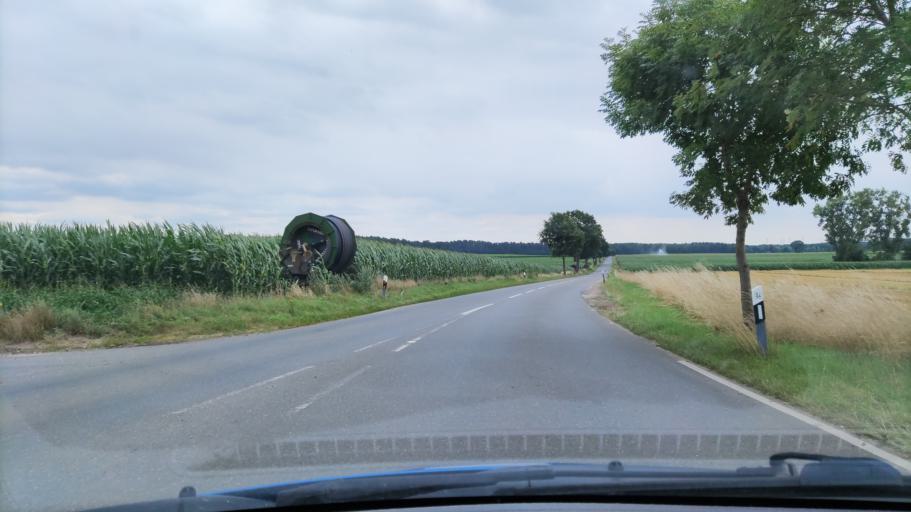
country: DE
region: Lower Saxony
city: Stoetze
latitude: 53.0287
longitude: 10.7659
